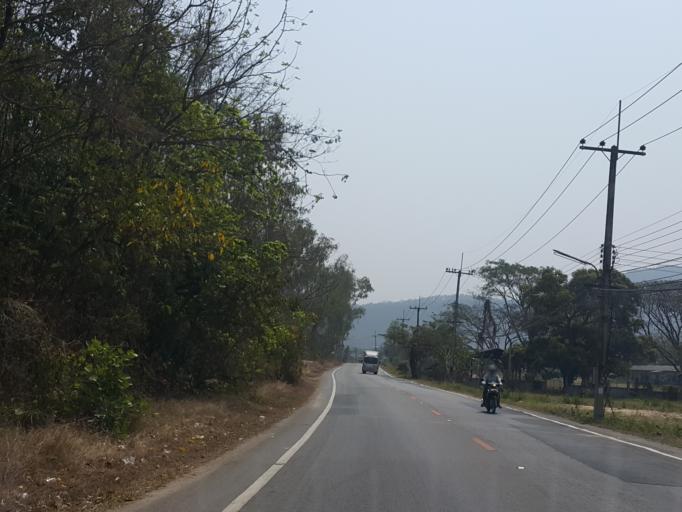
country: TH
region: Chiang Mai
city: San Kamphaeng
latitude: 18.7240
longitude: 99.1725
